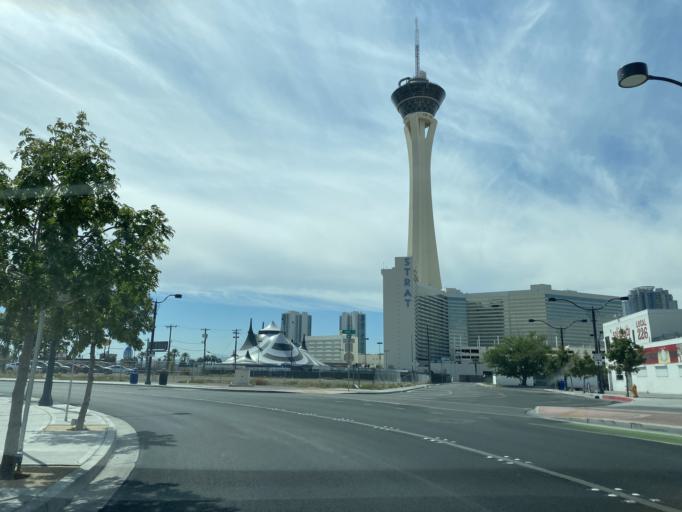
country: US
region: Nevada
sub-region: Clark County
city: Las Vegas
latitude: 36.1515
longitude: -115.1556
